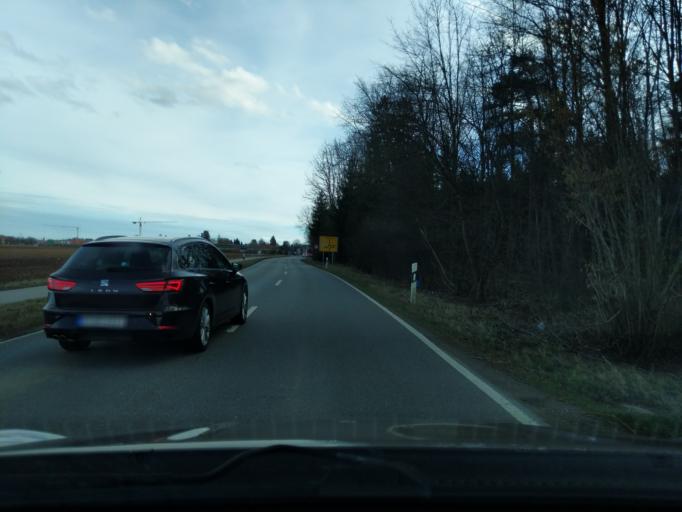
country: DE
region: Bavaria
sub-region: Upper Bavaria
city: Vaterstetten
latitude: 48.1192
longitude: 11.7677
